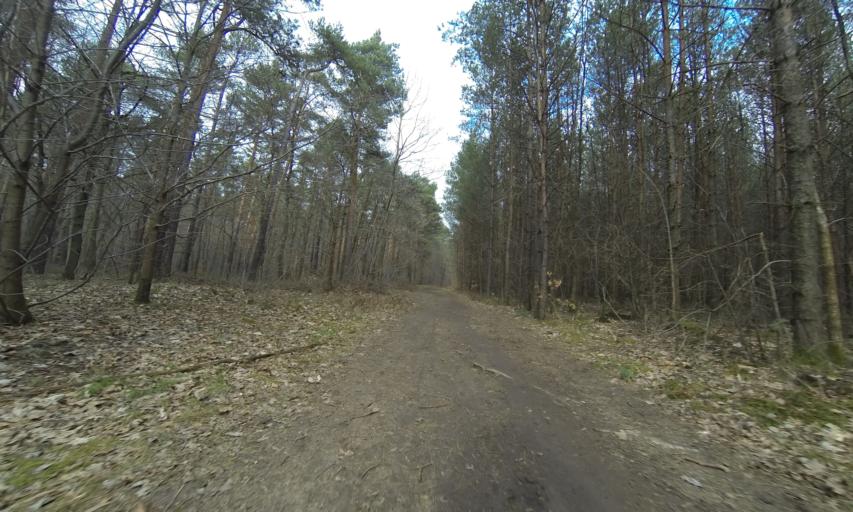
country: DE
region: Saxony
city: Radebeul
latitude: 51.1044
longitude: 13.6994
